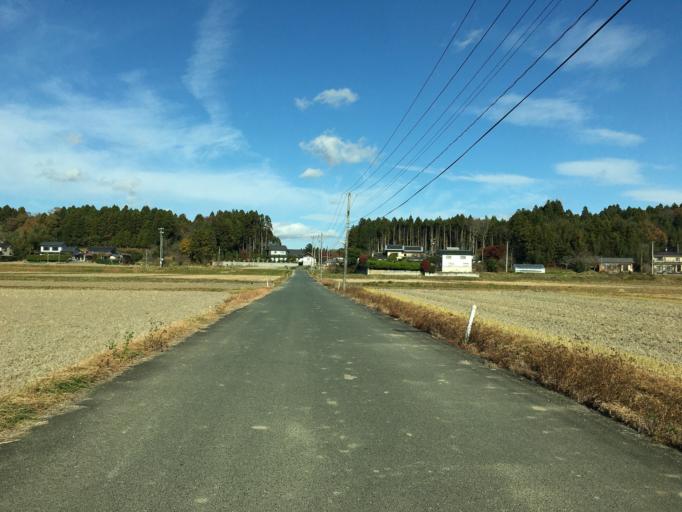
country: JP
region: Miyagi
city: Marumori
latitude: 37.8923
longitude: 140.9115
